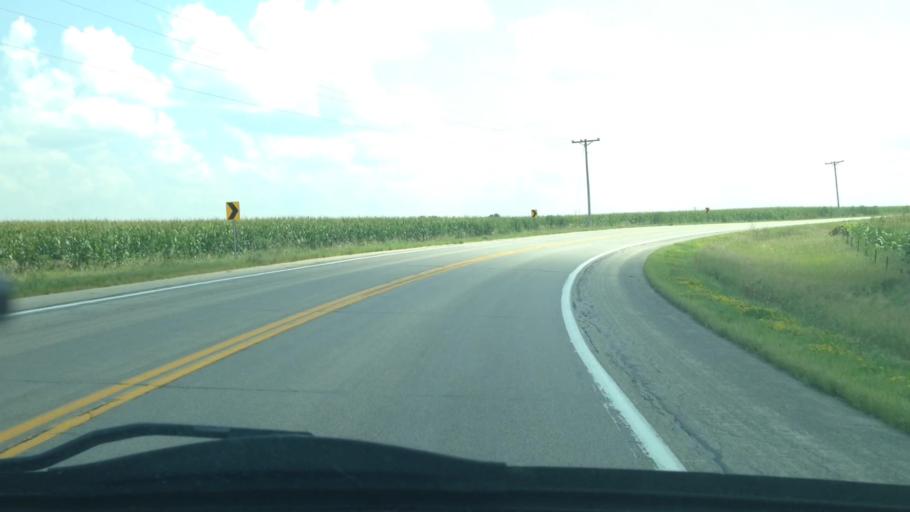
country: US
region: Minnesota
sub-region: Olmsted County
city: Rochester
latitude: 43.9452
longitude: -92.4092
